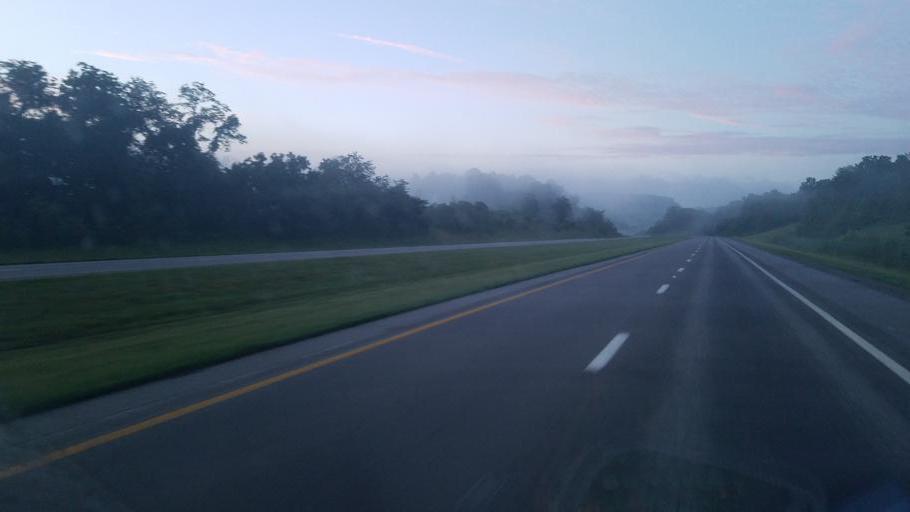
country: US
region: Ohio
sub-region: Ross County
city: Chillicothe
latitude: 39.2483
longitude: -82.8483
